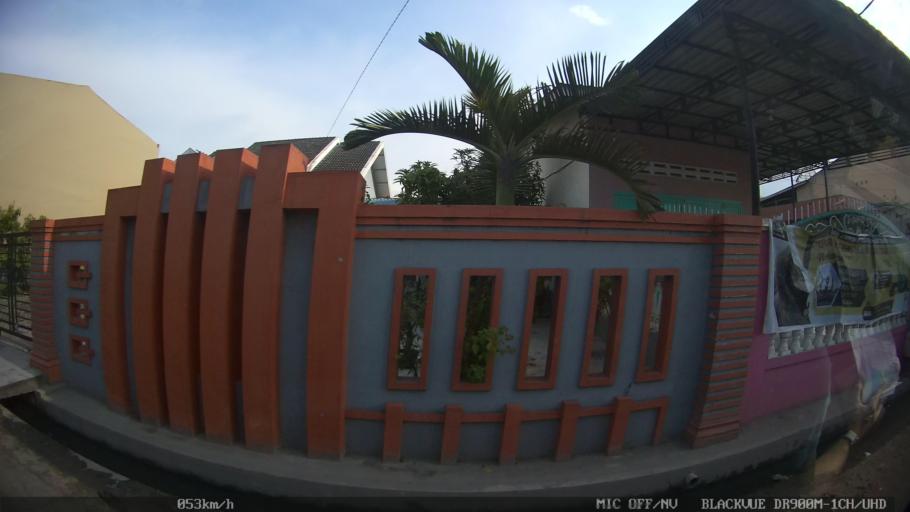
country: ID
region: North Sumatra
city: Percut
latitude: 3.5940
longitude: 98.7686
